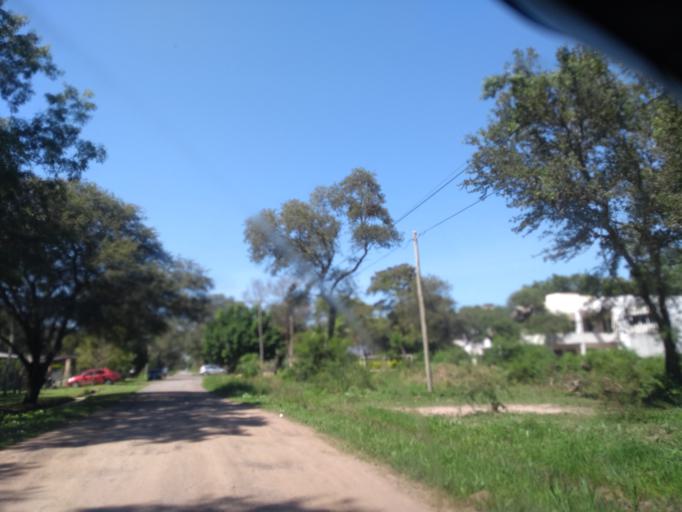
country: AR
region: Chaco
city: Resistencia
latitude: -27.4296
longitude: -58.9449
